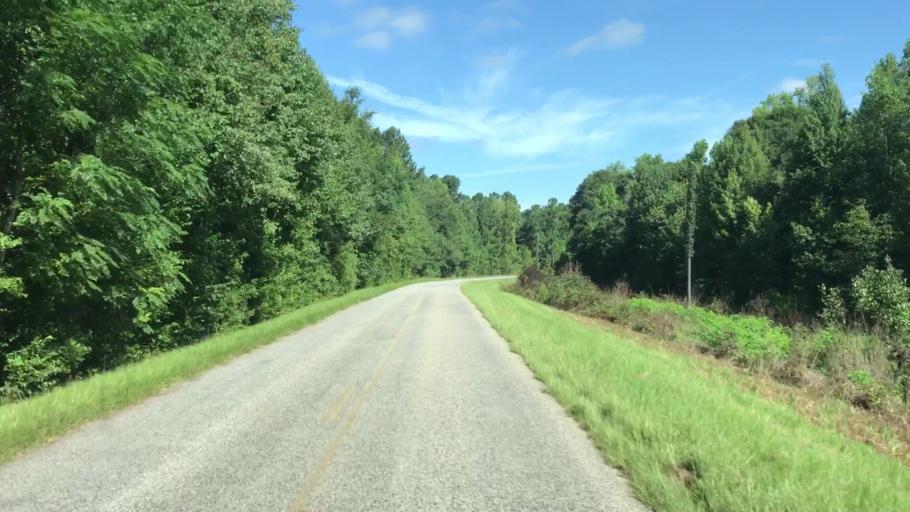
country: US
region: Georgia
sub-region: Jefferson County
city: Wadley
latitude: 32.8104
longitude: -82.3744
